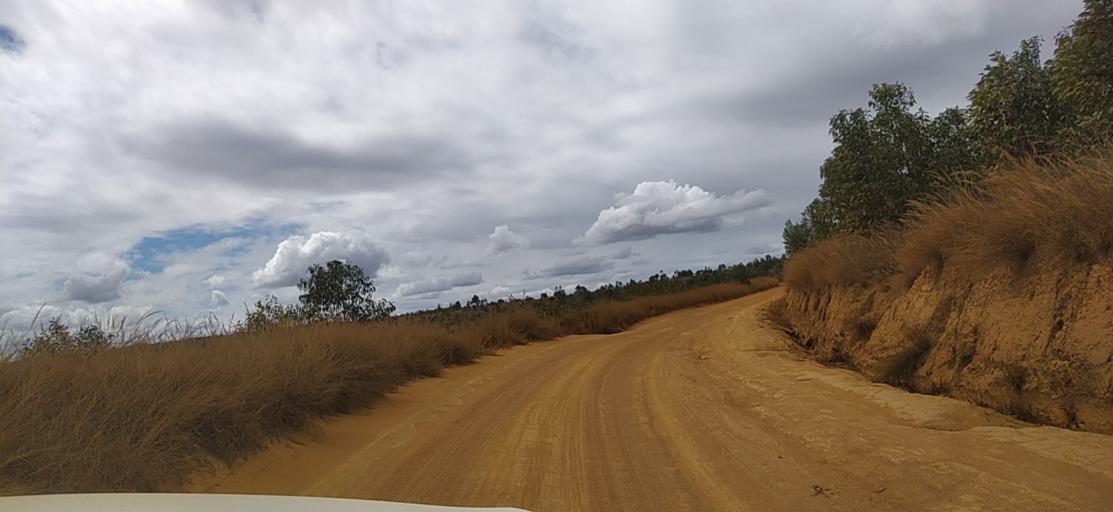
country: MG
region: Alaotra Mangoro
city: Ambatondrazaka
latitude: -17.9522
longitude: 48.2485
